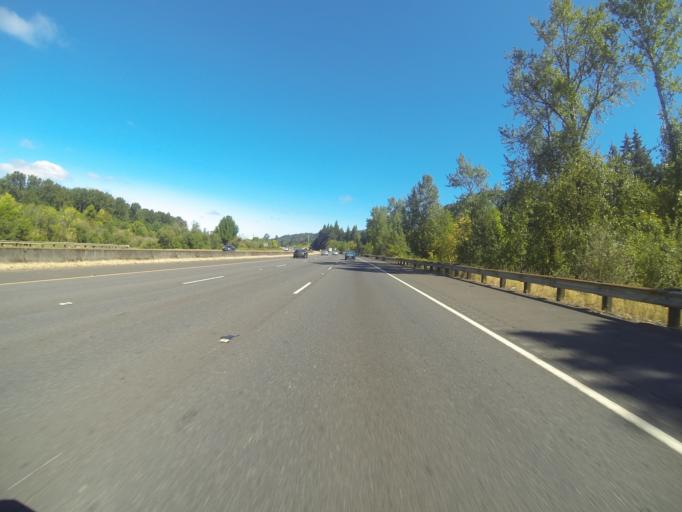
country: US
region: Oregon
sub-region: Columbia County
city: Rainier
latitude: 46.0781
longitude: -122.8663
